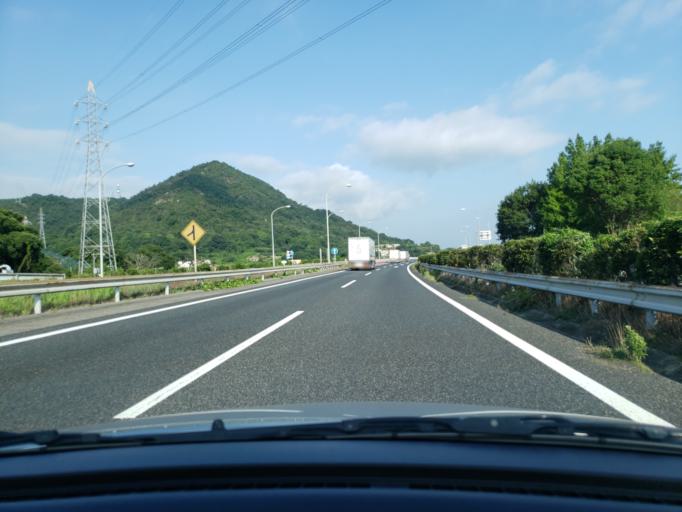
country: JP
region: Hiroshima
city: Fukuyama
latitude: 34.5137
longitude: 133.3953
